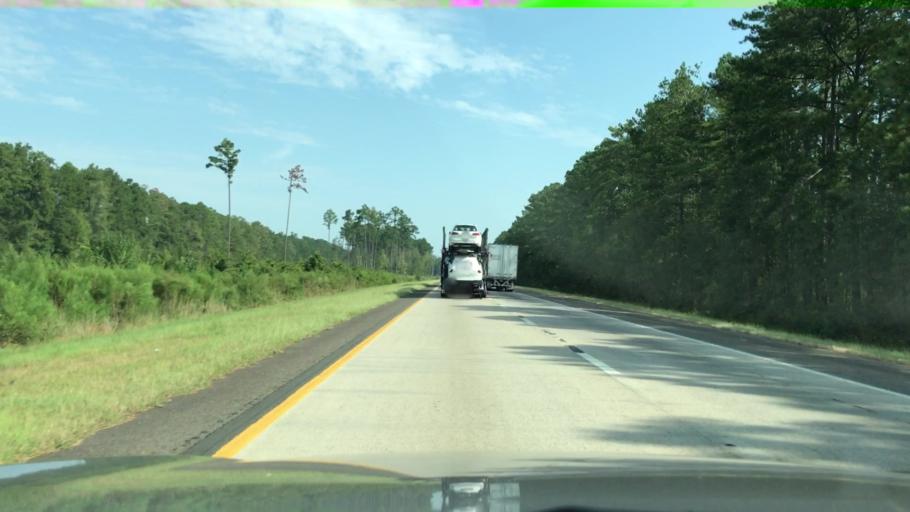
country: US
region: South Carolina
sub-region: Colleton County
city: Walterboro
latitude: 32.8521
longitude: -80.7326
